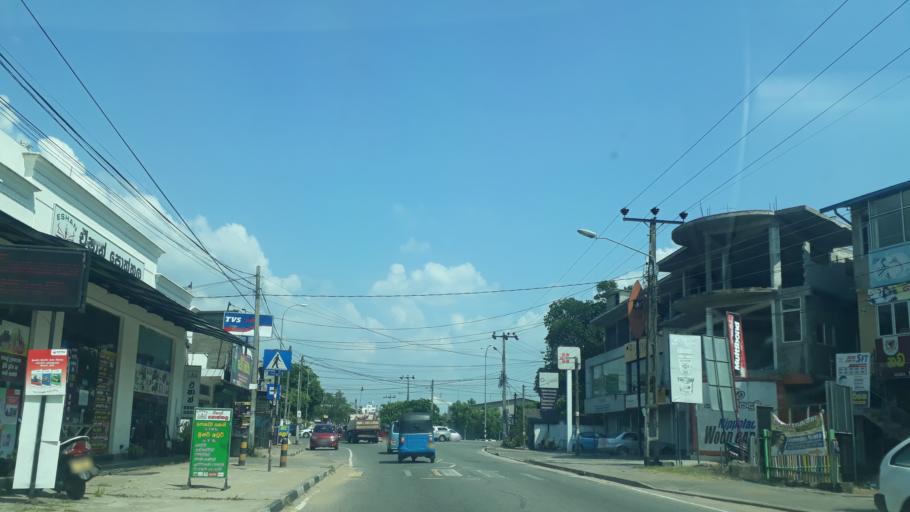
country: LK
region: Western
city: Gampaha
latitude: 7.0928
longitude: 79.9896
